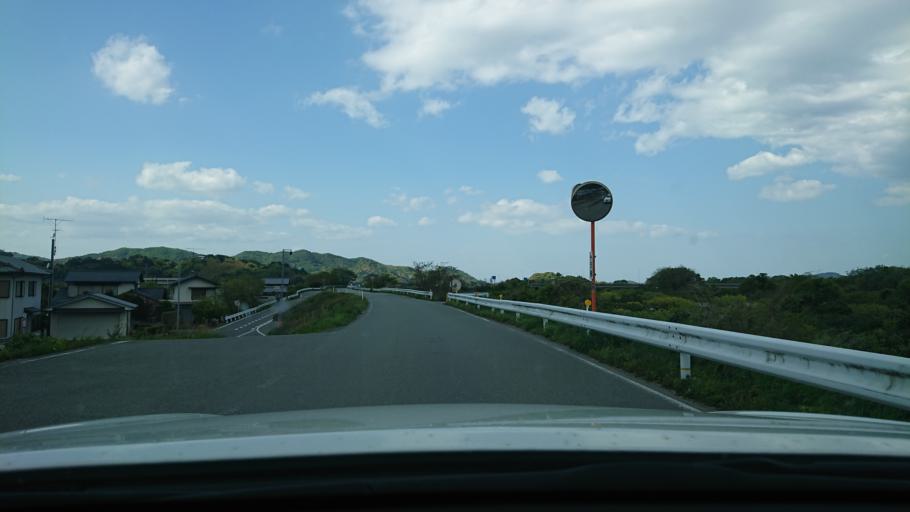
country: JP
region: Tokushima
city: Komatsushimacho
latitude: 33.9913
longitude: 134.5464
